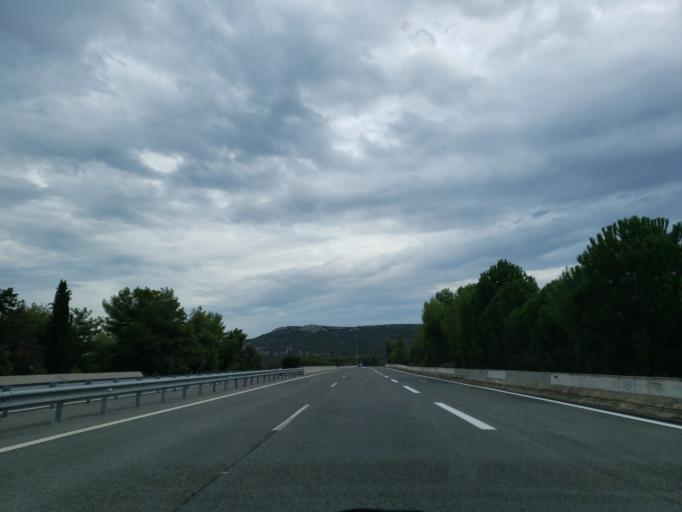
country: GR
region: Central Greece
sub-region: Nomos Voiotias
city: Akraifnia
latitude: 38.4053
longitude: 23.2193
